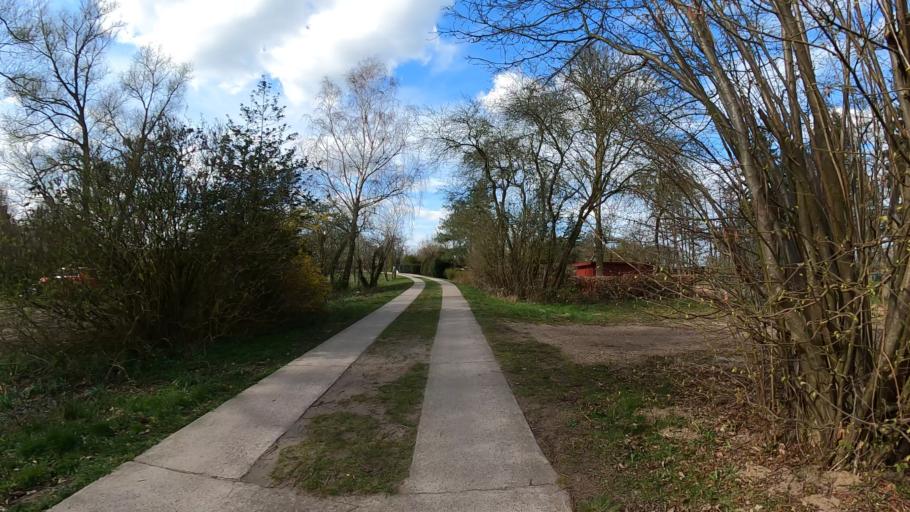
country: DE
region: Lower Saxony
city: Winsen
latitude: 53.4130
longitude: 10.1886
